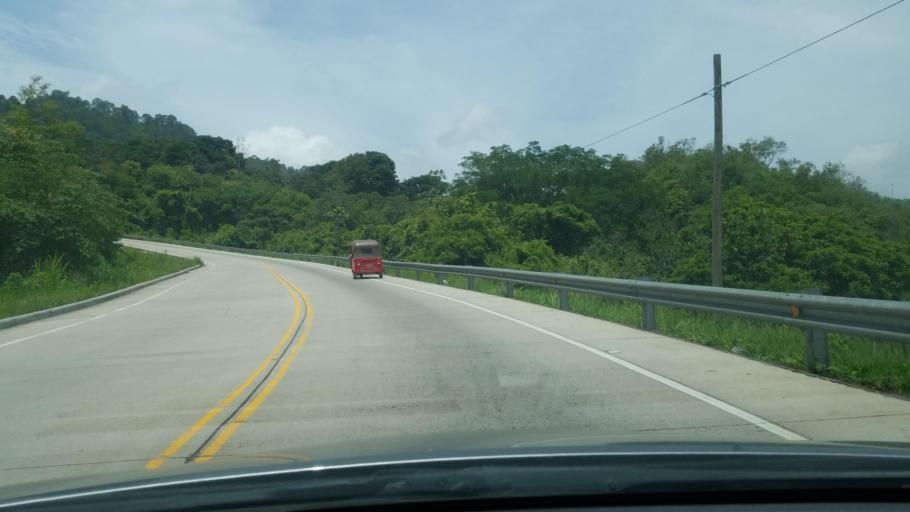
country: HN
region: Copan
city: Agua Caliente
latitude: 14.8788
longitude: -88.7802
